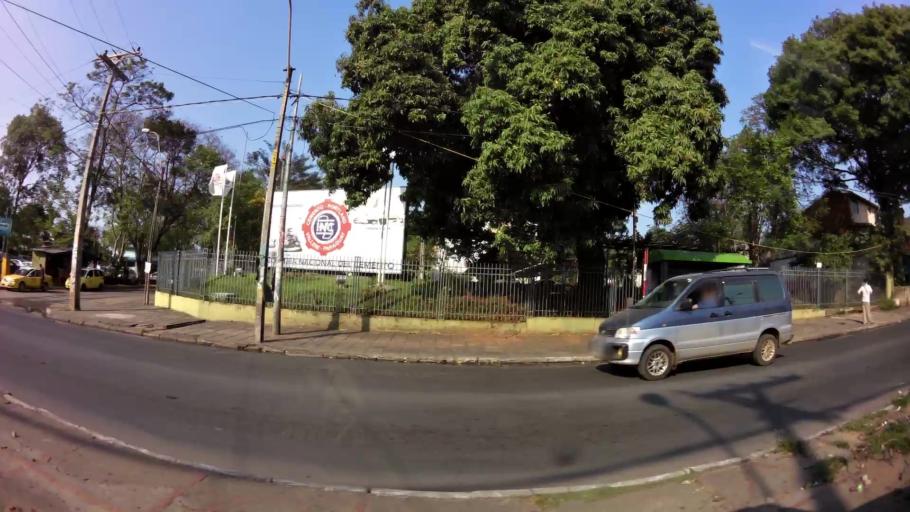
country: PY
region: Central
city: Lambare
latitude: -25.3179
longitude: -57.6069
